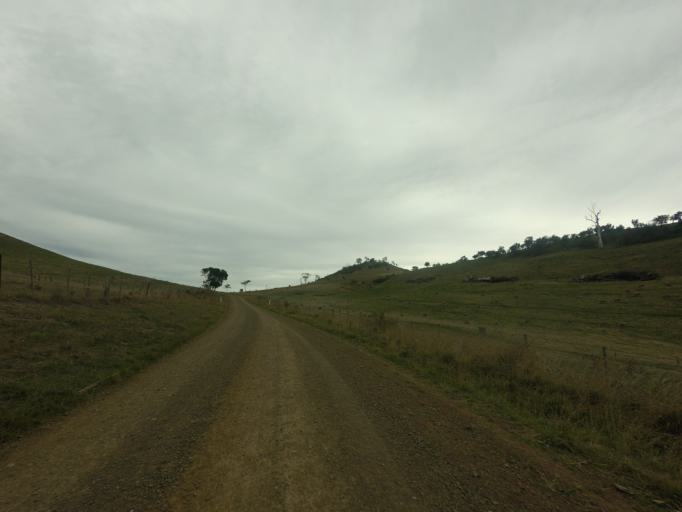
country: AU
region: Tasmania
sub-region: Derwent Valley
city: New Norfolk
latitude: -42.3752
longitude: 146.8631
